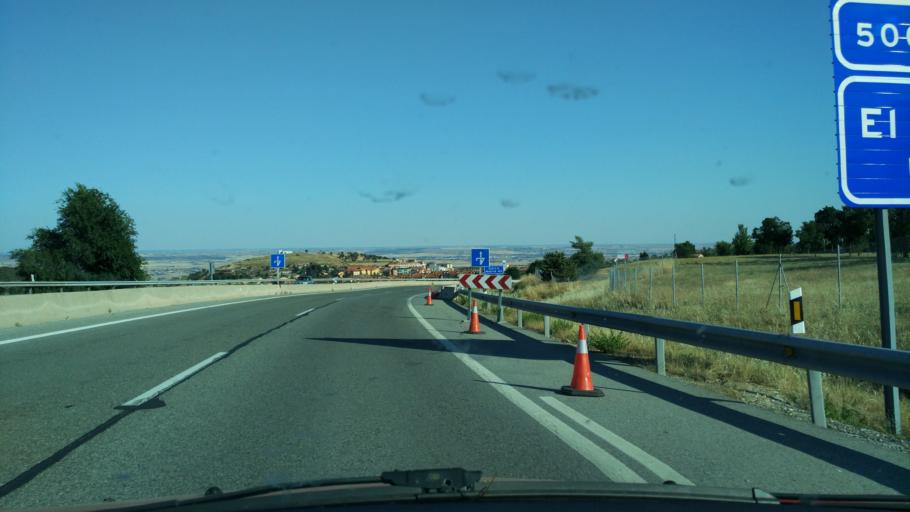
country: ES
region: Madrid
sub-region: Provincia de Madrid
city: Pedrezuela
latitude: 40.7429
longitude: -3.5892
